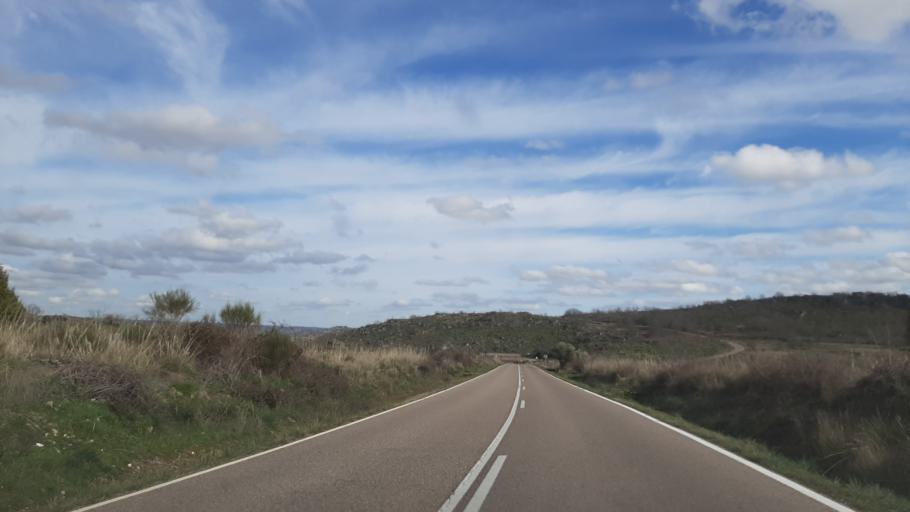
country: ES
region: Castille and Leon
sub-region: Provincia de Salamanca
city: Villarino de los Aires
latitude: 41.2635
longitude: -6.4402
